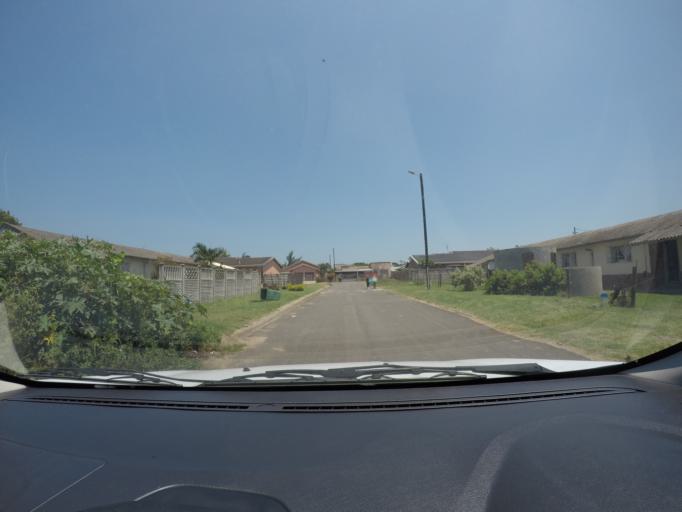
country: ZA
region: KwaZulu-Natal
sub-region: uThungulu District Municipality
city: eSikhawini
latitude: -28.8916
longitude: 31.8865
